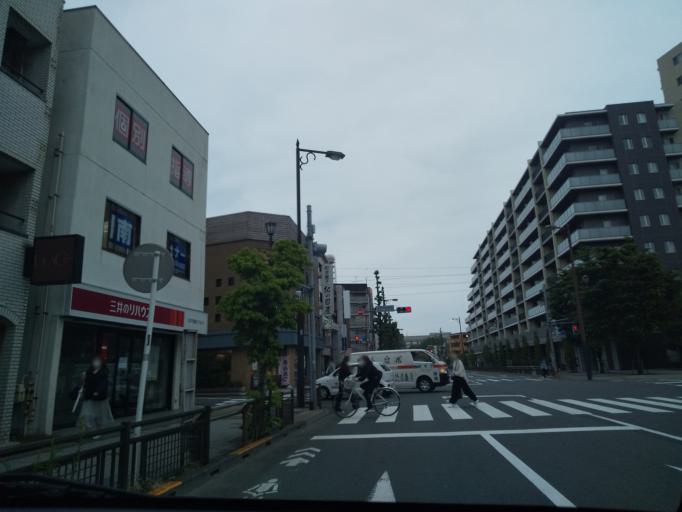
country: JP
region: Tokyo
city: Hino
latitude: 35.6622
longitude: 139.3796
